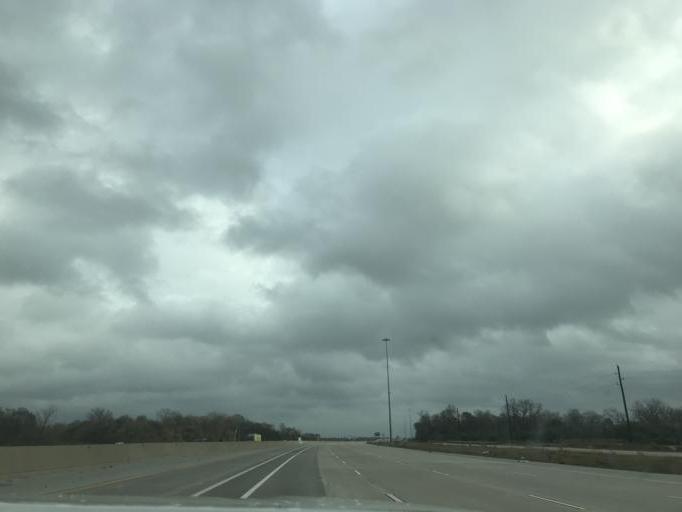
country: US
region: Texas
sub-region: Fort Bend County
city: Richmond
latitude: 29.5524
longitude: -95.7346
